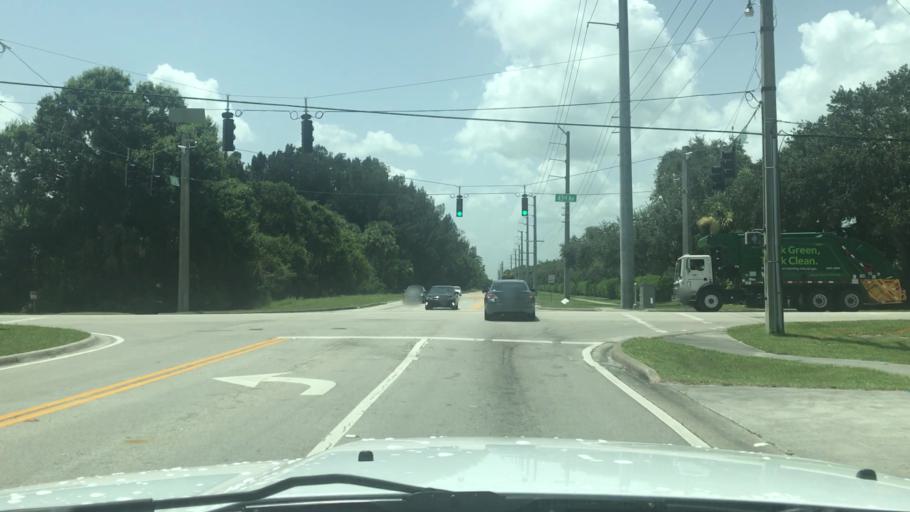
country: US
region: Florida
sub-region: Indian River County
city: Vero Beach South
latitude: 27.6239
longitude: -80.4300
